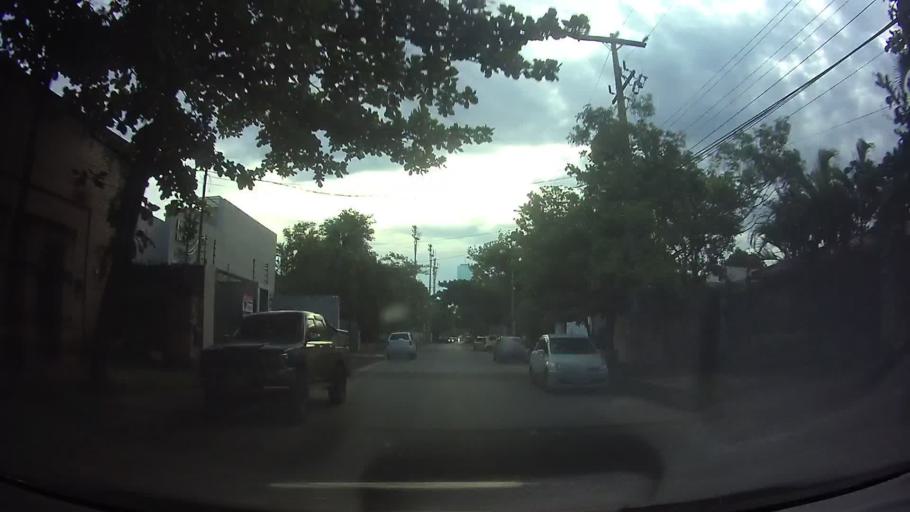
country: PY
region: Central
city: Fernando de la Mora
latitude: -25.2746
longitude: -57.5513
